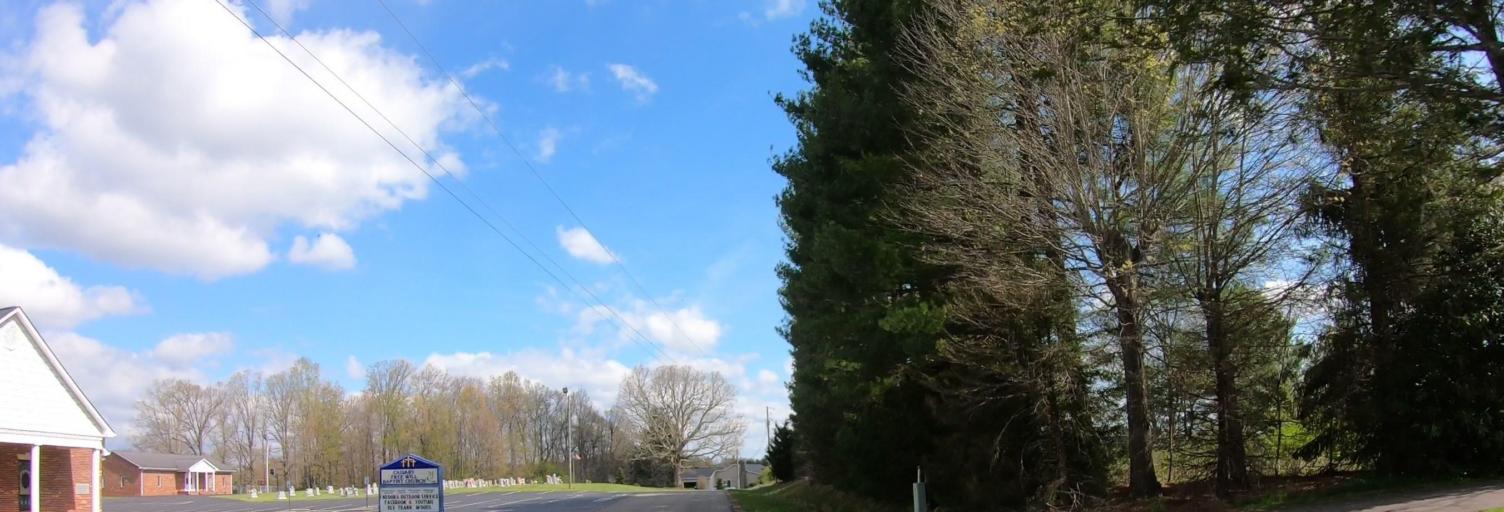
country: US
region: North Carolina
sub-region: Ashe County
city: Jefferson
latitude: 36.3523
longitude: -81.3802
